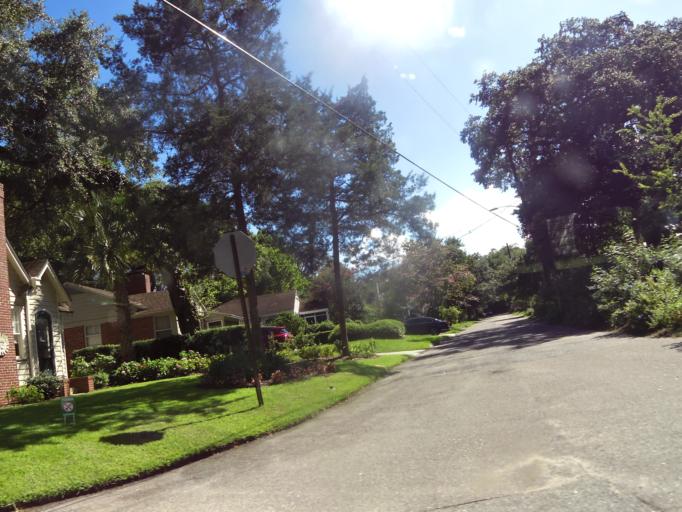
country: US
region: Florida
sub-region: Duval County
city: Jacksonville
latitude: 30.2984
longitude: -81.7152
